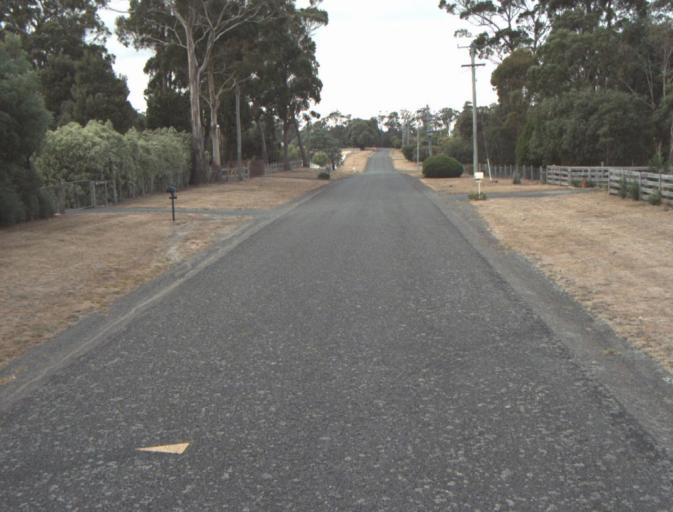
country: AU
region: Tasmania
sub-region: Launceston
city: Mayfield
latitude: -41.3254
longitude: 147.0556
